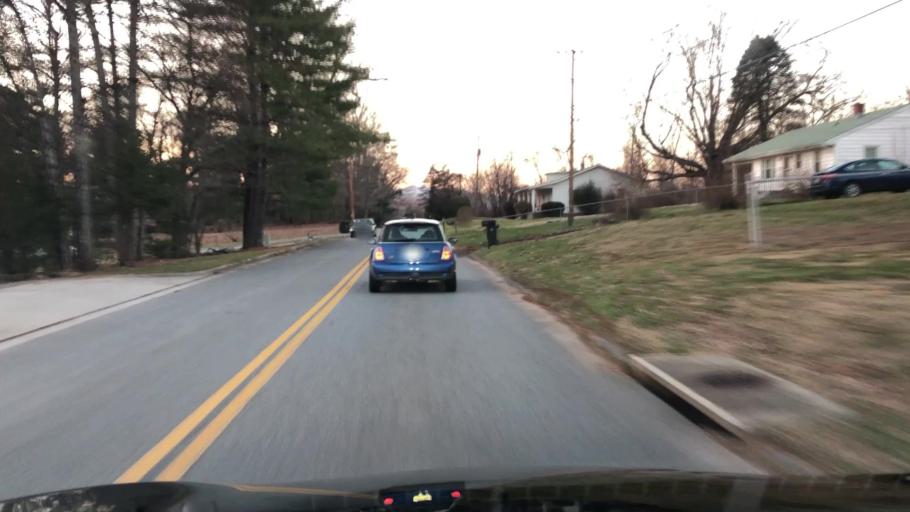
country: US
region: Virginia
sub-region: City of Lynchburg
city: West Lynchburg
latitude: 37.4071
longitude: -79.2209
